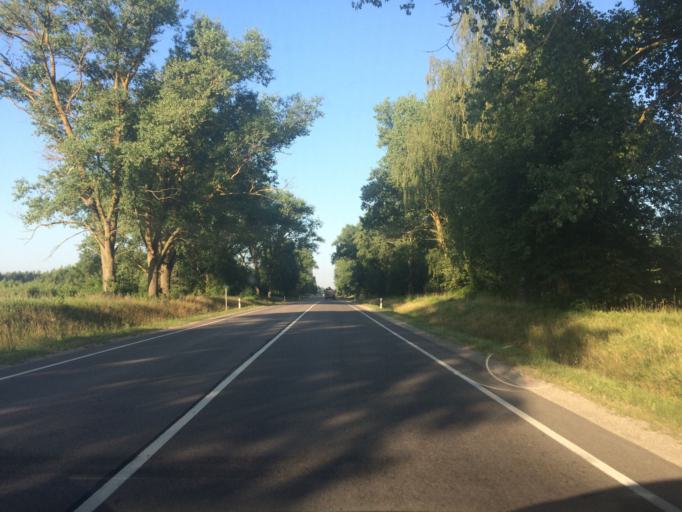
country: LT
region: Vilnius County
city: Ukmerge
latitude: 55.3004
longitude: 24.8574
